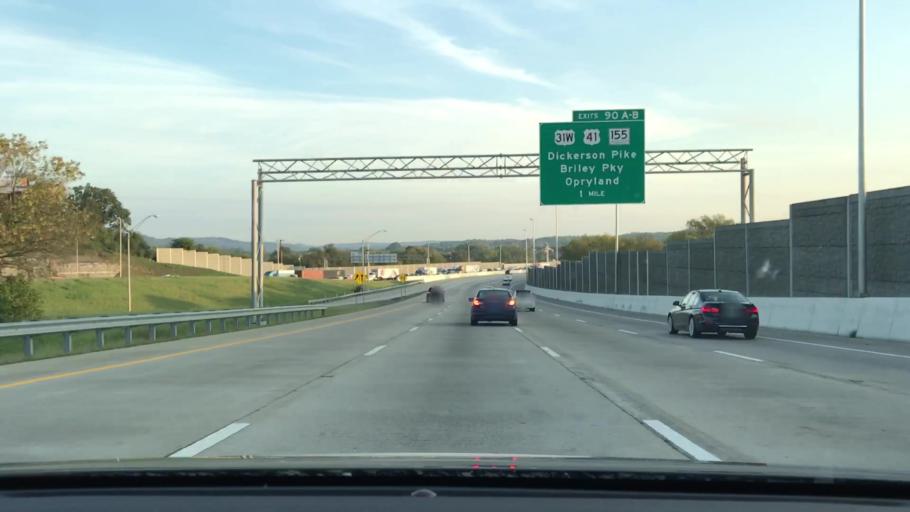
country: US
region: Tennessee
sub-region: Davidson County
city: Nashville
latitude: 36.2257
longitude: -86.7729
